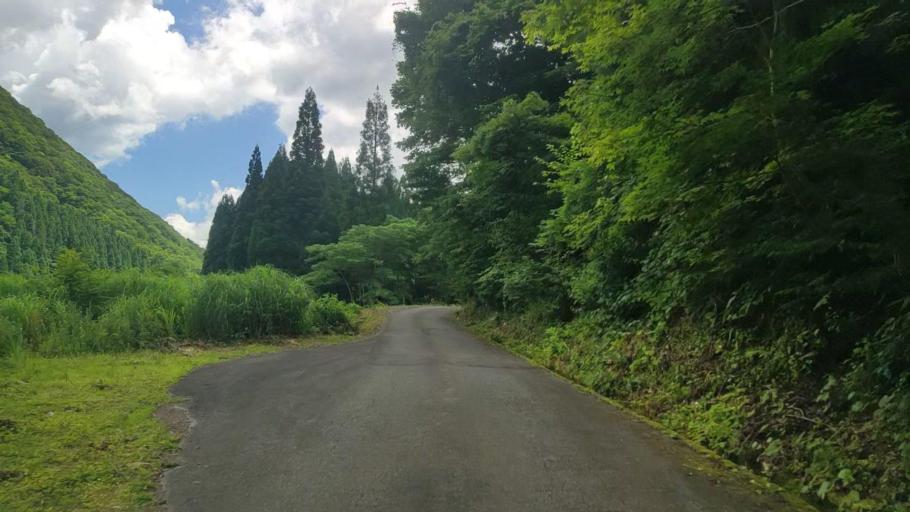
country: JP
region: Fukui
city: Ono
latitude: 35.8132
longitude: 136.4609
